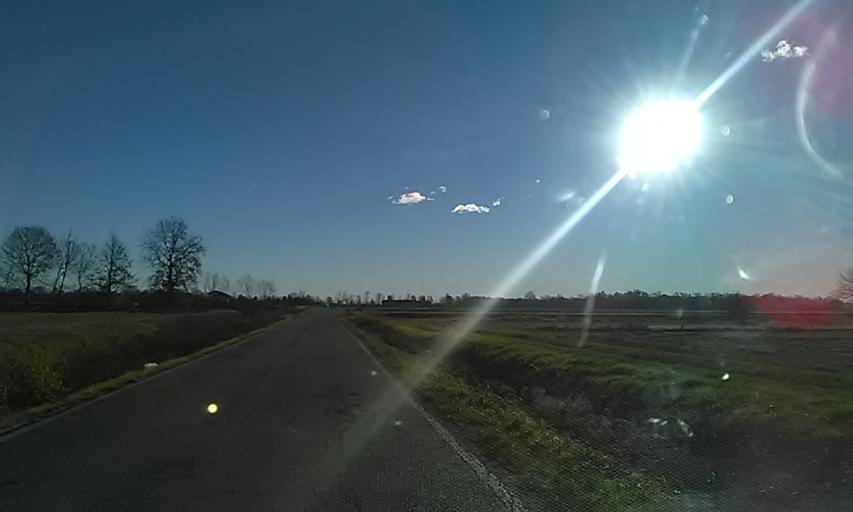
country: IT
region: Piedmont
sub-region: Provincia di Vercelli
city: Rovasenda
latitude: 45.5443
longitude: 8.2823
